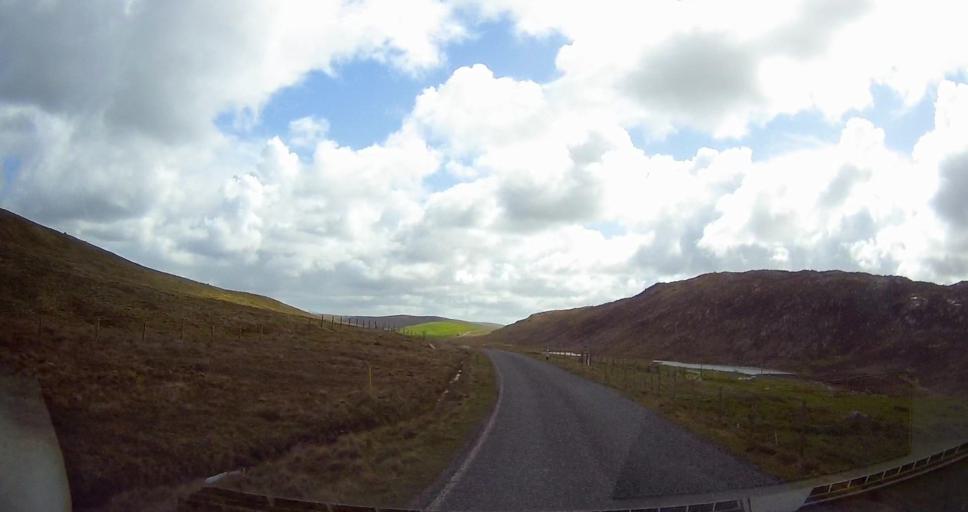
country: GB
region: Scotland
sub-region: Shetland Islands
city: Lerwick
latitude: 60.5569
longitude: -1.3378
